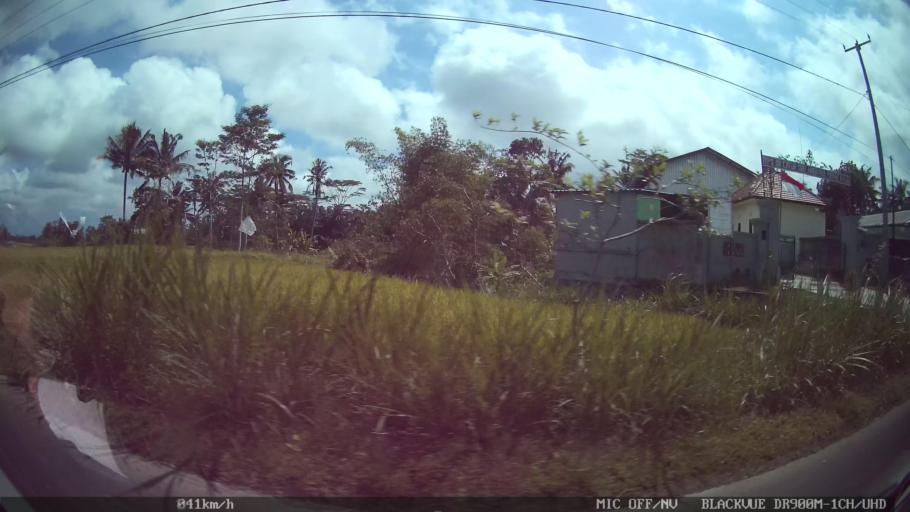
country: ID
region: Bali
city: Banjar Abuan
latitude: -8.4600
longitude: 115.3220
